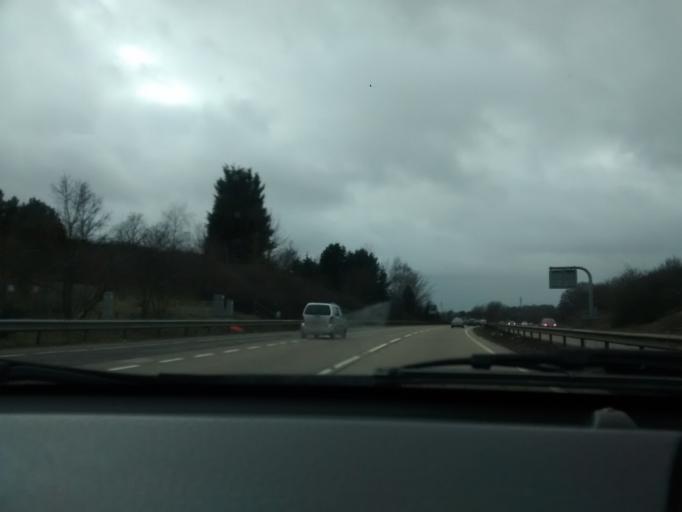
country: GB
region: England
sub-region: Suffolk
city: Ipswich
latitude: 52.0240
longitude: 1.1862
